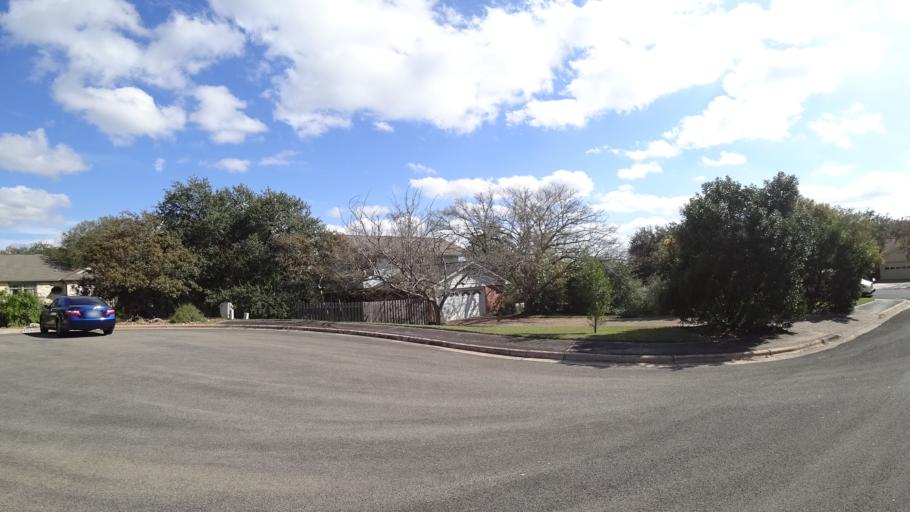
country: US
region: Texas
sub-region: Williamson County
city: Anderson Mill
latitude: 30.4234
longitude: -97.8045
